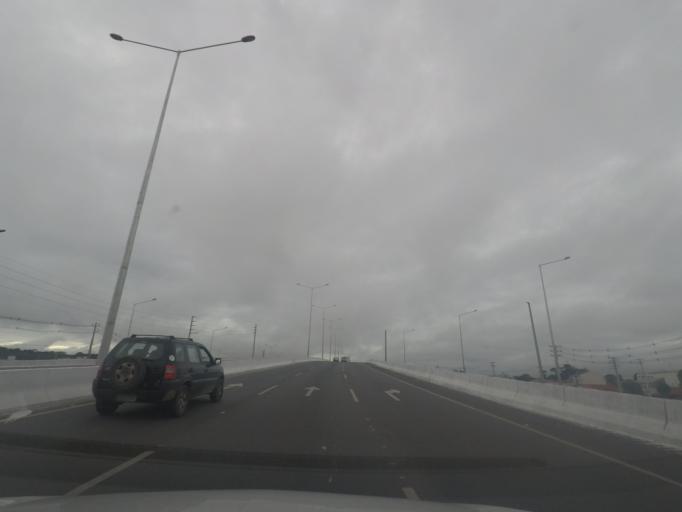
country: BR
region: Parana
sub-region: Pinhais
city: Pinhais
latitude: -25.4375
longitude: -49.1643
